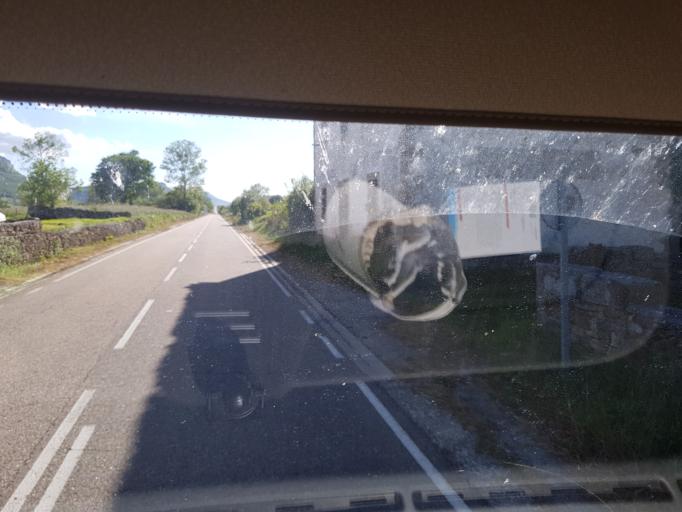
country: ES
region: Castille and Leon
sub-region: Provincia de Burgos
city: Espinosa de los Monteros
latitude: 43.0631
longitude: -3.5837
